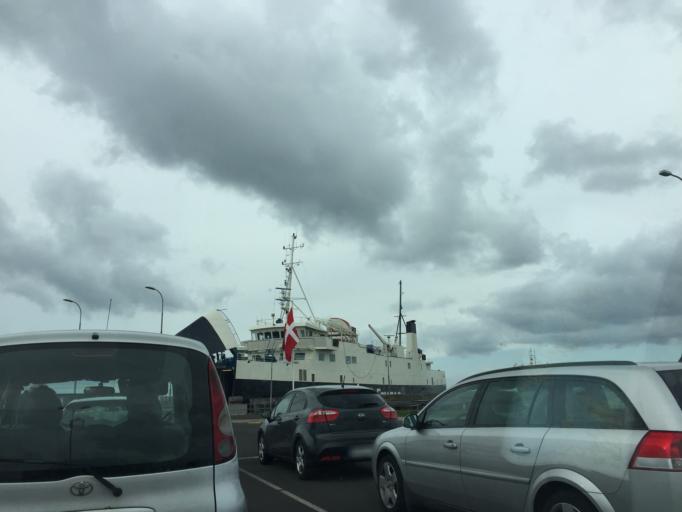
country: DK
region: South Denmark
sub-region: Assens Kommune
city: Harby
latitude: 55.1046
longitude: 10.0831
